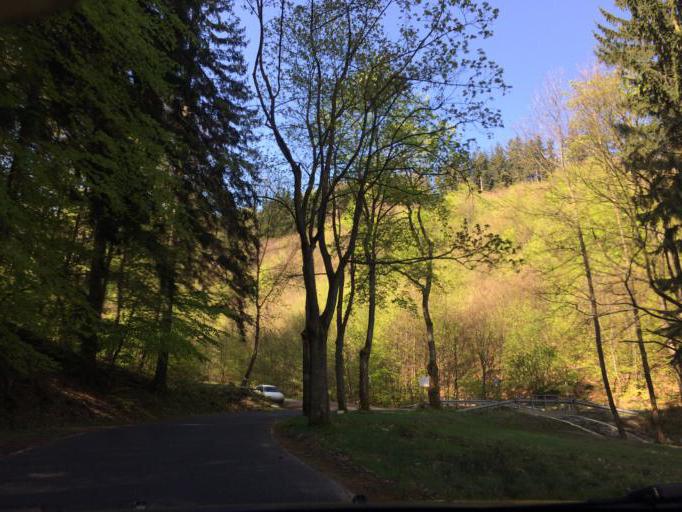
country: PL
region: Lower Silesian Voivodeship
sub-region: Powiat klodzki
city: Jugow
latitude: 50.6629
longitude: 16.5391
